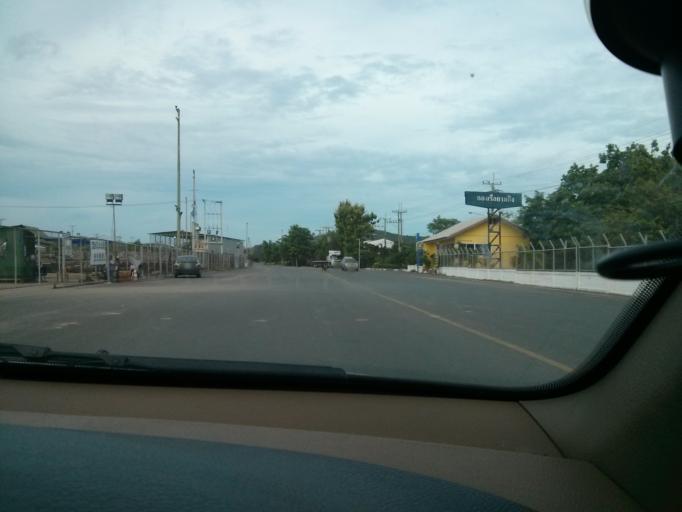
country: TH
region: Chon Buri
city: Sattahip
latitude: 12.6248
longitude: 100.9152
